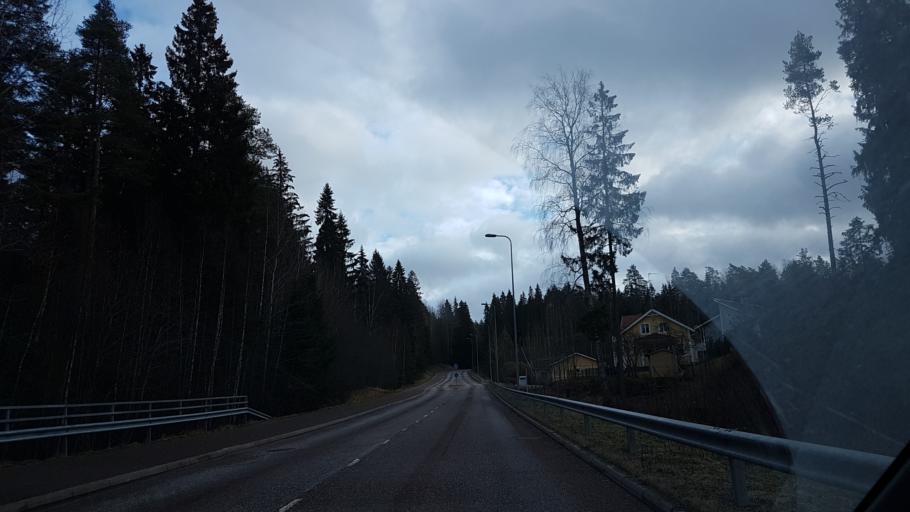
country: FI
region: Uusimaa
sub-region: Helsinki
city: Kauniainen
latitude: 60.3277
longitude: 24.7206
